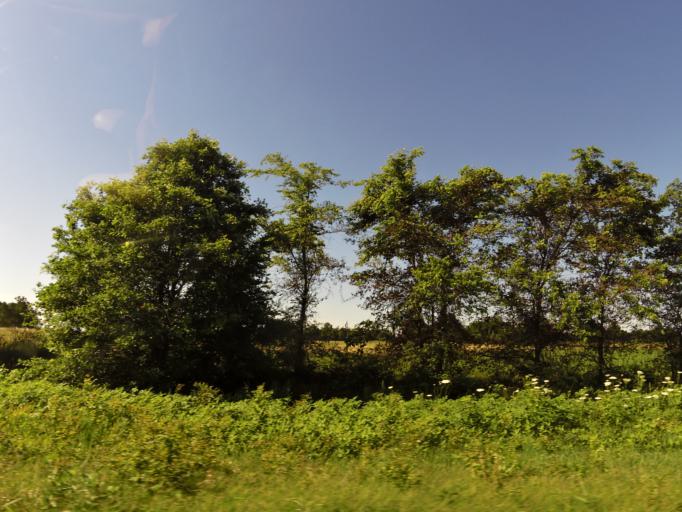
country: US
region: Arkansas
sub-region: Clay County
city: Corning
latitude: 36.4000
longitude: -90.5117
